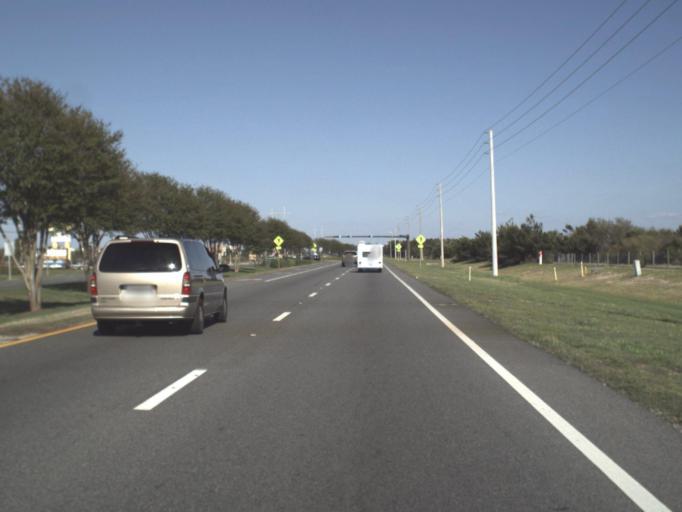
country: US
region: Florida
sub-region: Okaloosa County
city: Destin
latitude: 30.3869
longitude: -86.4453
